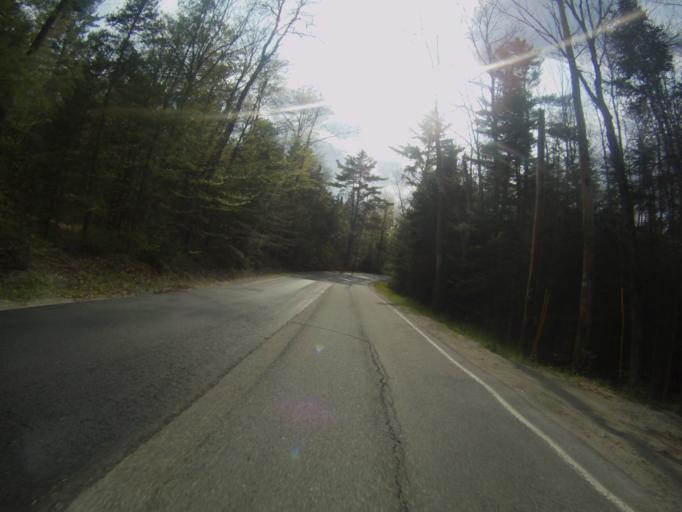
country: US
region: New York
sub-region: Warren County
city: Warrensburg
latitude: 43.8452
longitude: -73.8010
